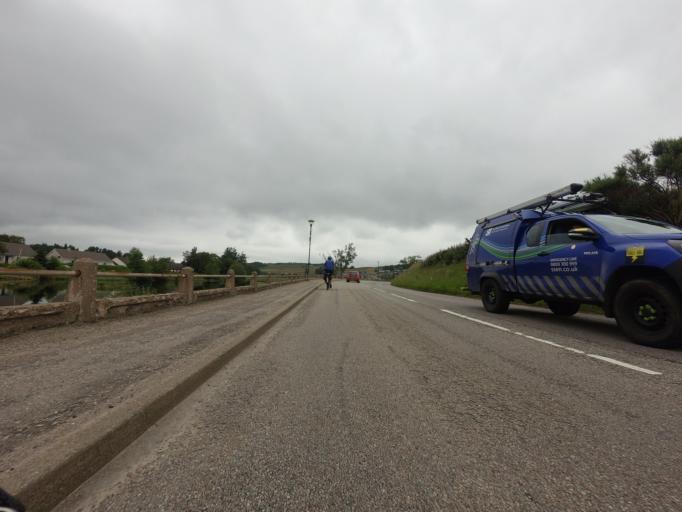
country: GB
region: Scotland
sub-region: Highland
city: Alness
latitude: 58.0211
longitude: -4.4042
